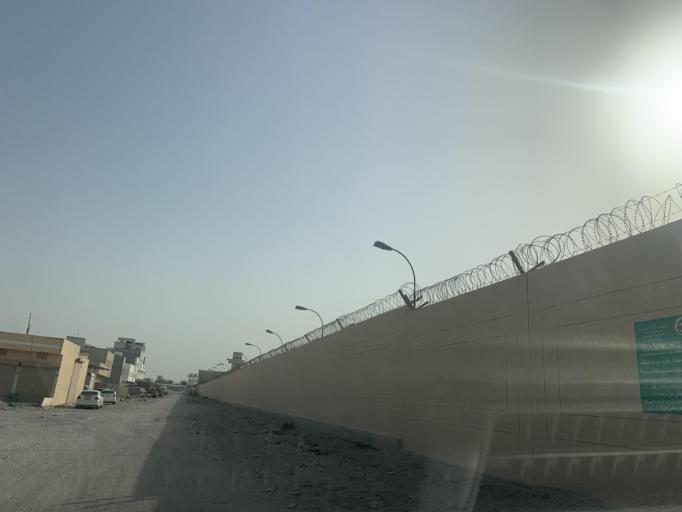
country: BH
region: Central Governorate
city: Madinat Hamad
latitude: 26.1463
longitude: 50.4829
